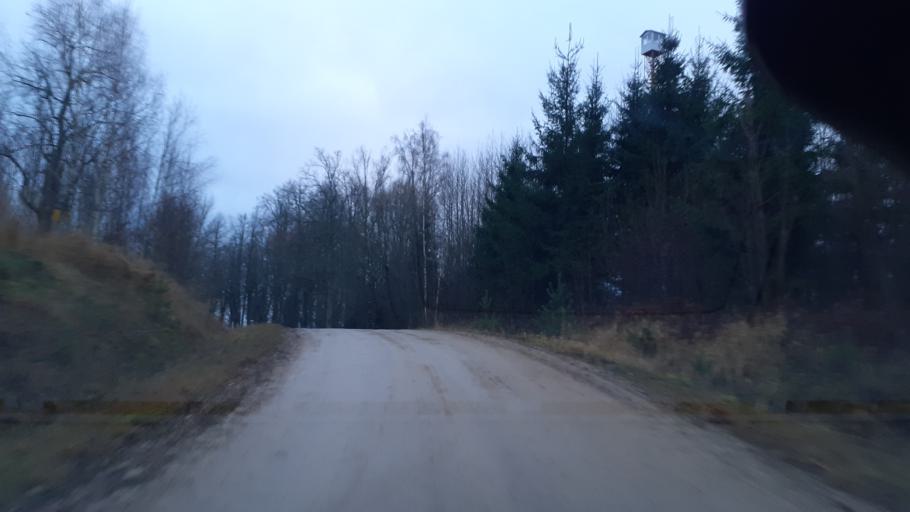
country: LV
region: Alsunga
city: Alsunga
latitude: 56.9085
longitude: 21.7126
